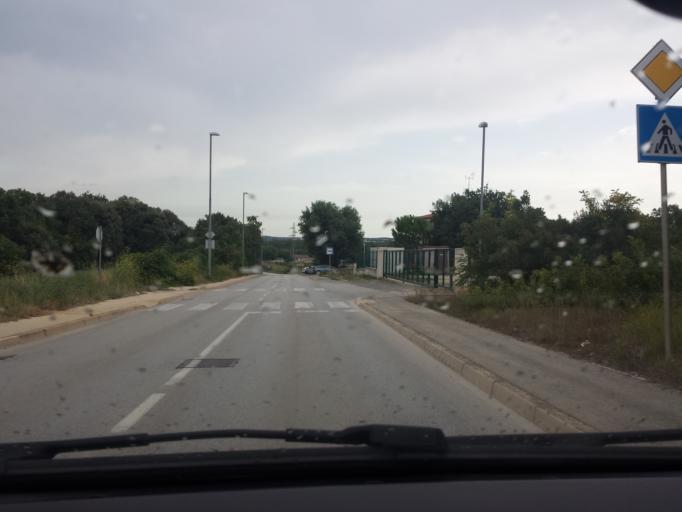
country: HR
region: Istarska
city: Galizana
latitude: 44.9053
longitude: 13.8546
